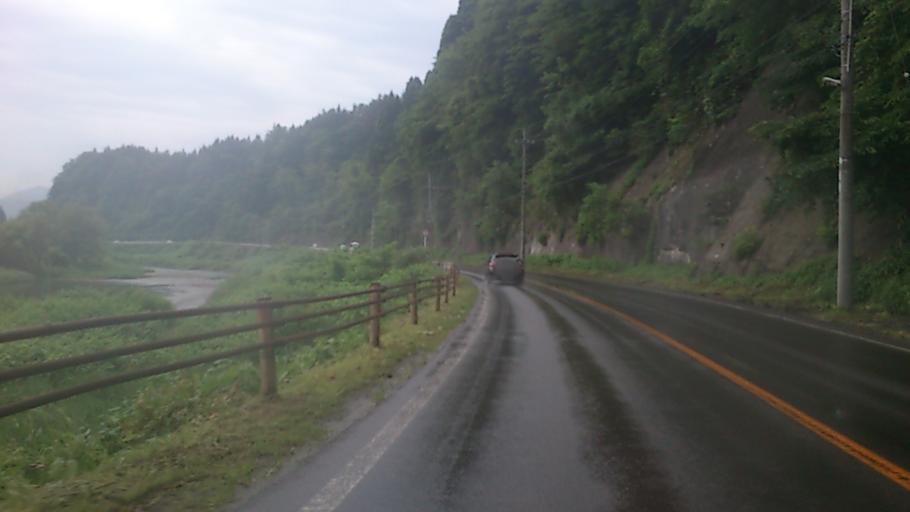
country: JP
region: Akita
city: Takanosu
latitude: 40.2384
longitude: 140.2430
